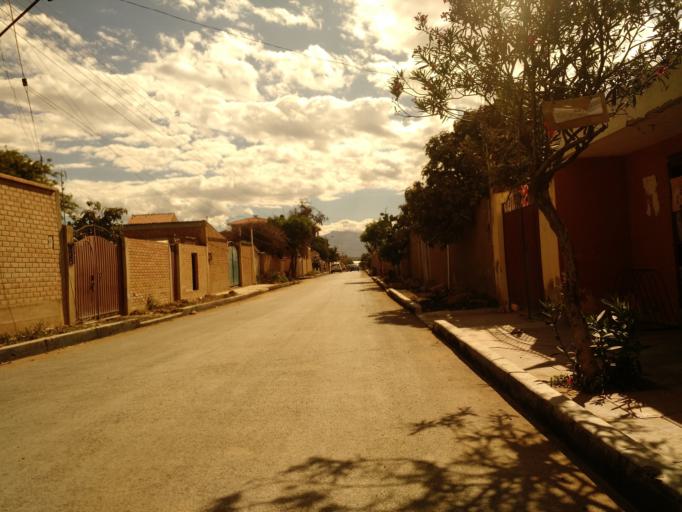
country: BO
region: Cochabamba
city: Cochabamba
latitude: -17.4587
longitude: -66.1504
